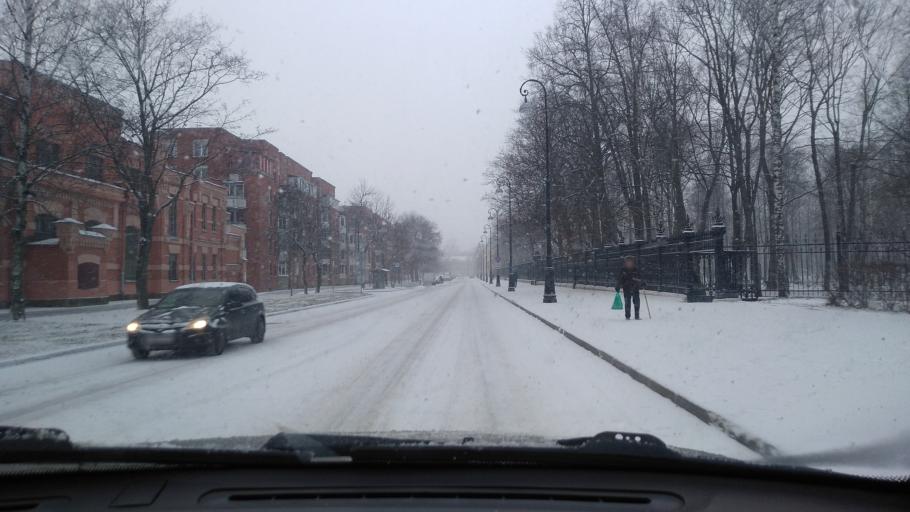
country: RU
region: St.-Petersburg
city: Kronshtadt
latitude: 59.9869
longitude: 29.7793
